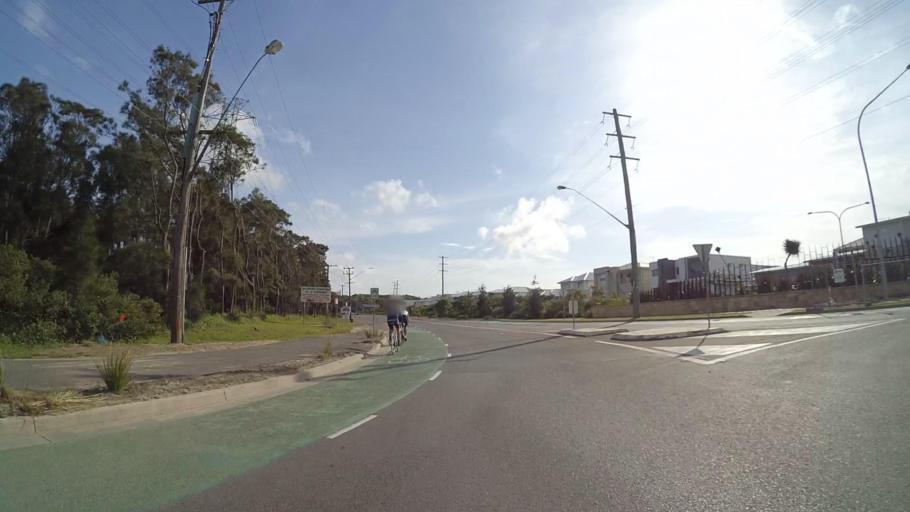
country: AU
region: New South Wales
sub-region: Sutherland Shire
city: Cronulla
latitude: -34.0362
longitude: 151.1601
